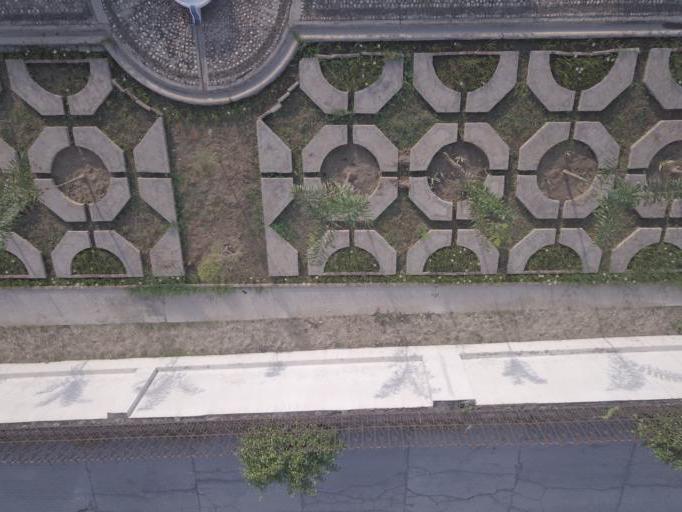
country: IN
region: Punjab
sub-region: Shahid Bhagat Singh Nagar
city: Rahon
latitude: 31.0207
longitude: 76.0927
